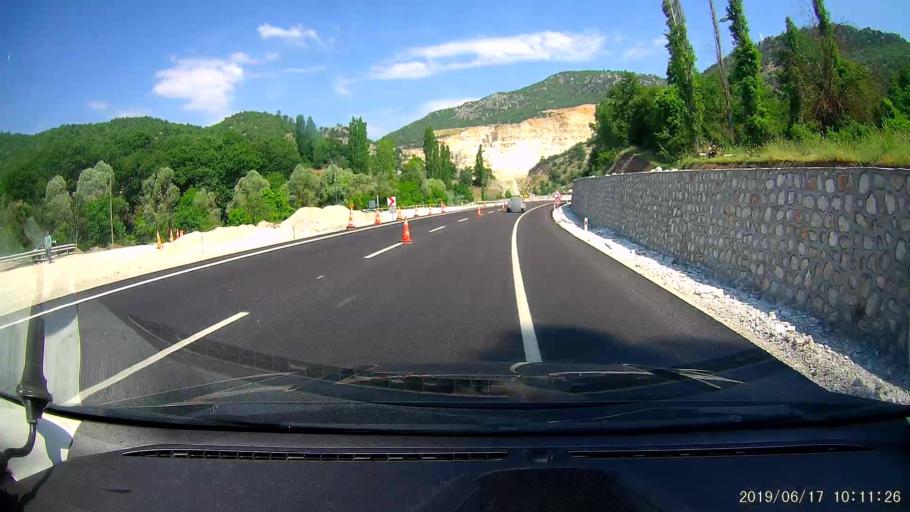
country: TR
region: Amasya
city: Saraycik
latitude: 40.9708
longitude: 35.0839
